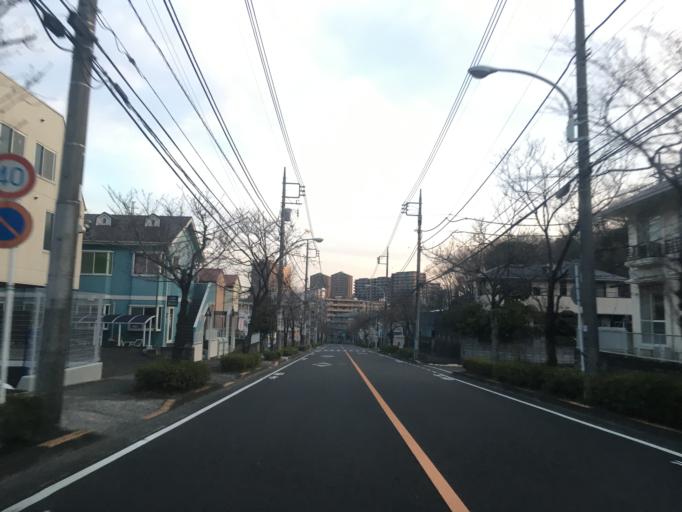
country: JP
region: Tokyo
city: Hino
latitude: 35.6069
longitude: 139.3856
